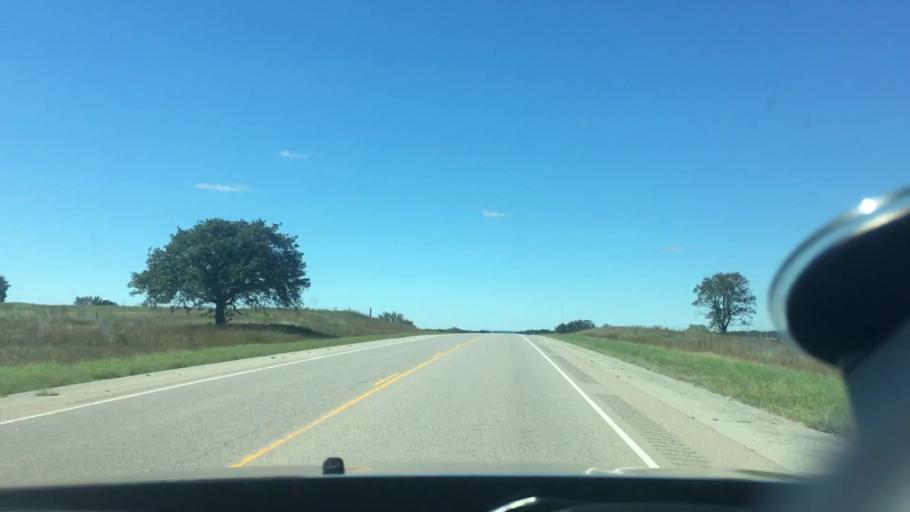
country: US
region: Oklahoma
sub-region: Coal County
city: Coalgate
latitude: 34.6182
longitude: -96.4494
